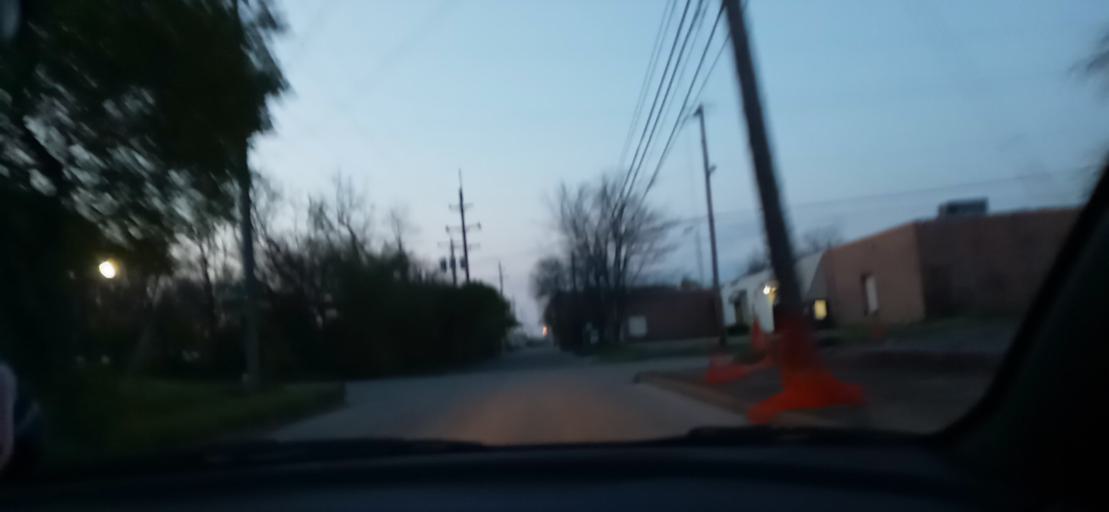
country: US
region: Ohio
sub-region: Summit County
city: Akron
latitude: 41.0541
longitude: -81.5248
